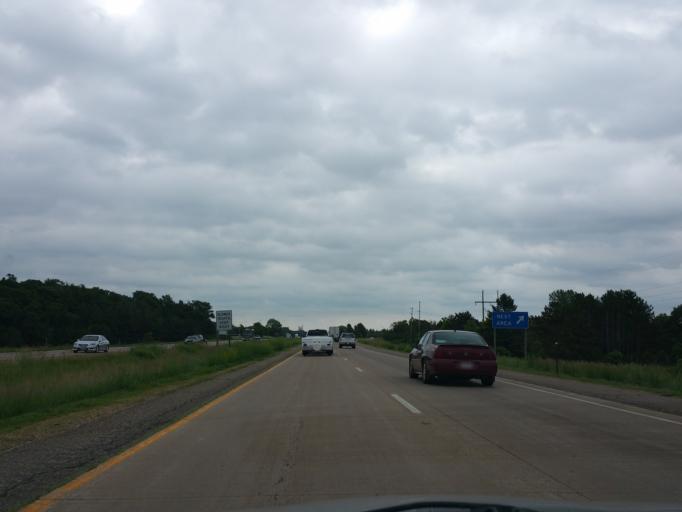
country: US
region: Wisconsin
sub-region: Dunn County
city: Menomonie
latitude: 44.9075
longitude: -91.9163
